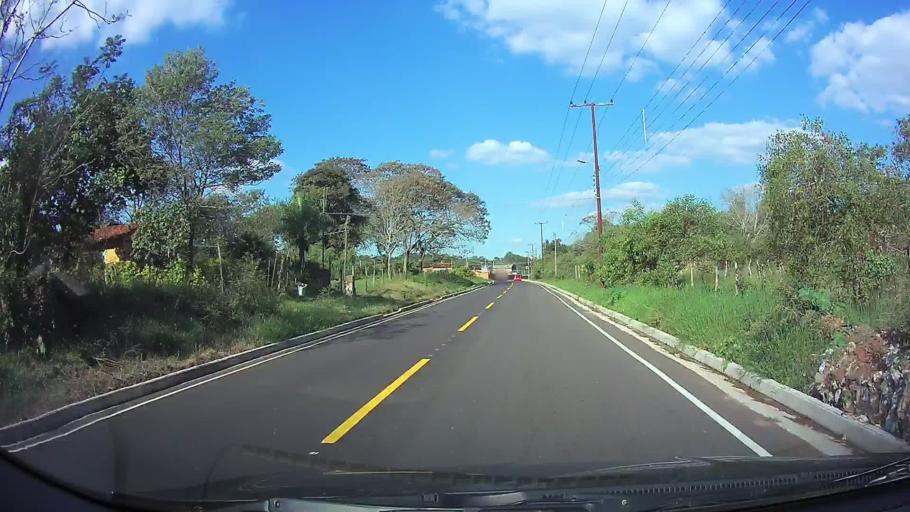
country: PY
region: Central
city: San Lorenzo
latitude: -25.2671
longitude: -57.4703
